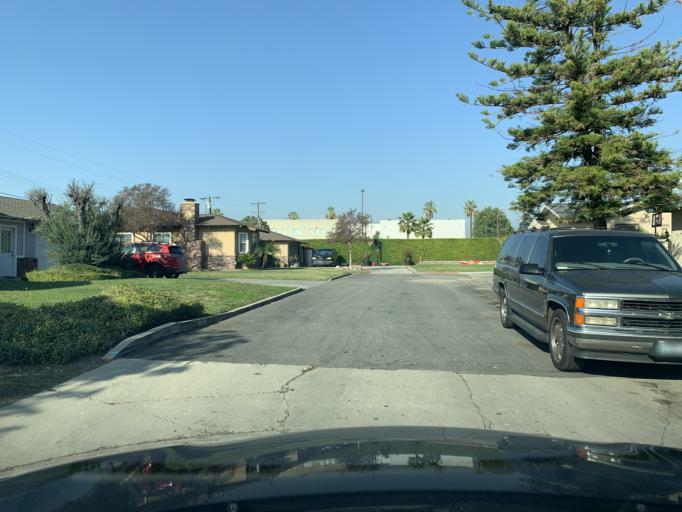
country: US
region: California
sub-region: Los Angeles County
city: Covina
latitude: 34.0772
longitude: -117.8971
